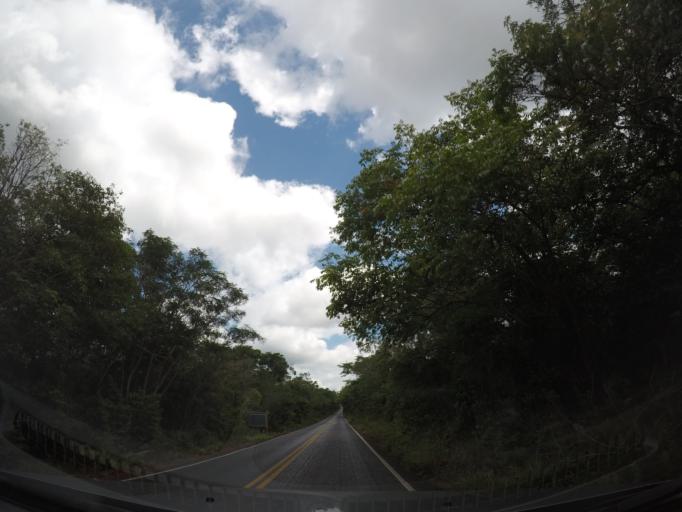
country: BR
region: Bahia
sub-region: Andarai
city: Vera Cruz
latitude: -12.5335
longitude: -41.3657
